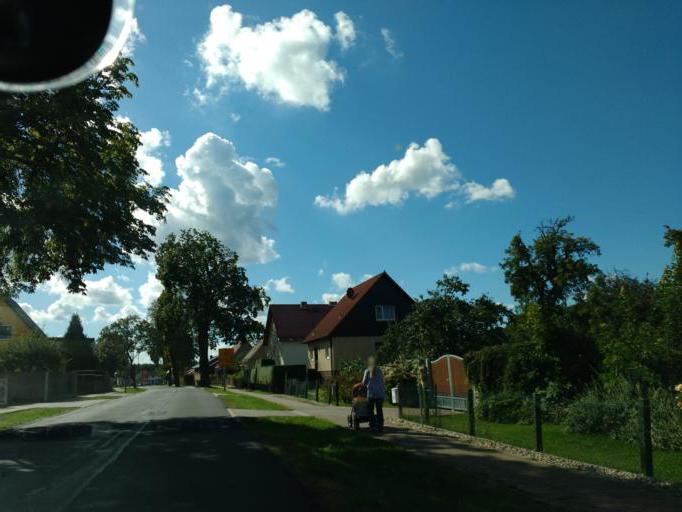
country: DE
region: Brandenburg
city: Mittenwalde
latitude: 52.2077
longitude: 13.5833
